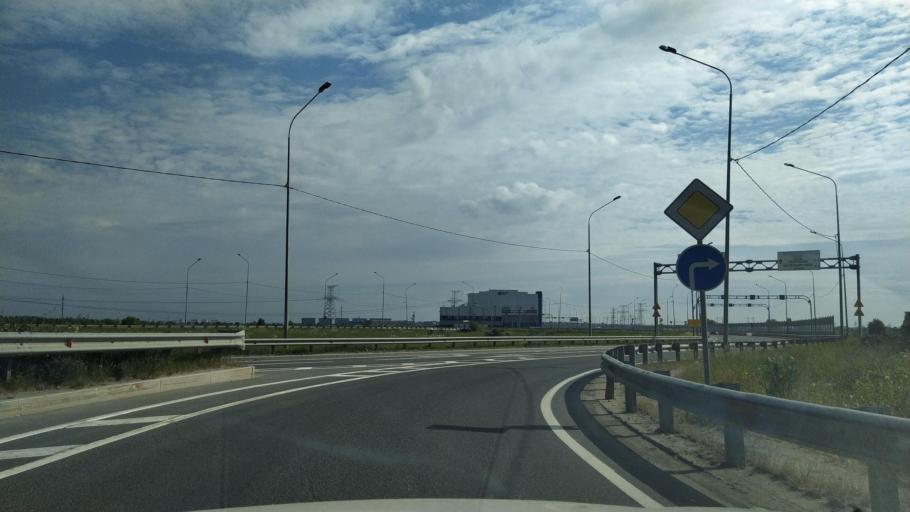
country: RU
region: St.-Petersburg
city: Aleksandrovskaya
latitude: 59.7402
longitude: 30.3228
